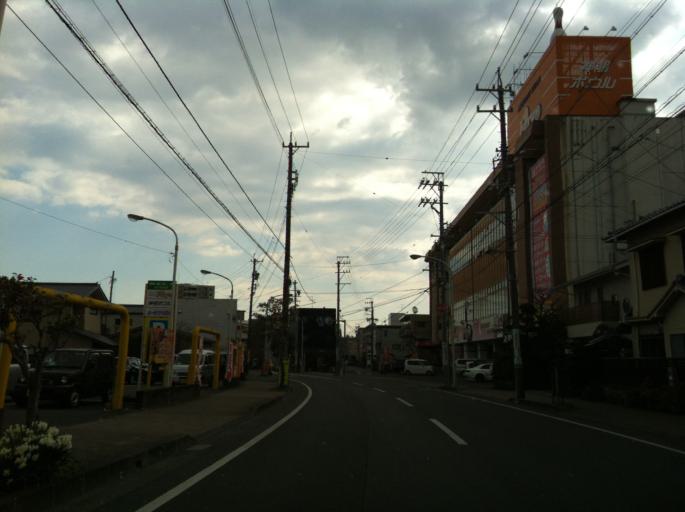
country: JP
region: Shizuoka
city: Shizuoka-shi
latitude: 34.9830
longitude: 138.3695
